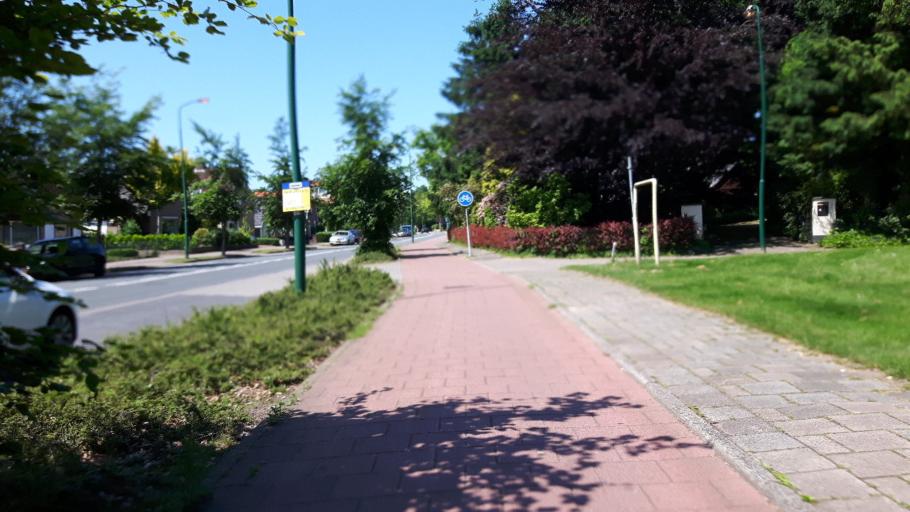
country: NL
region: Utrecht
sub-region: Gemeente Soest
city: Soest
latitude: 52.1753
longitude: 5.2912
